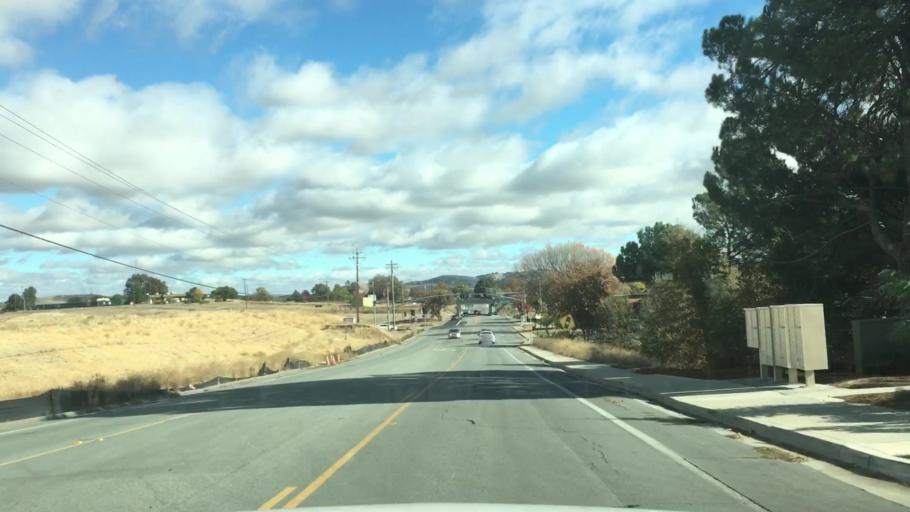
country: US
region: California
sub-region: San Luis Obispo County
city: Templeton
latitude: 35.5544
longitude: -120.7164
